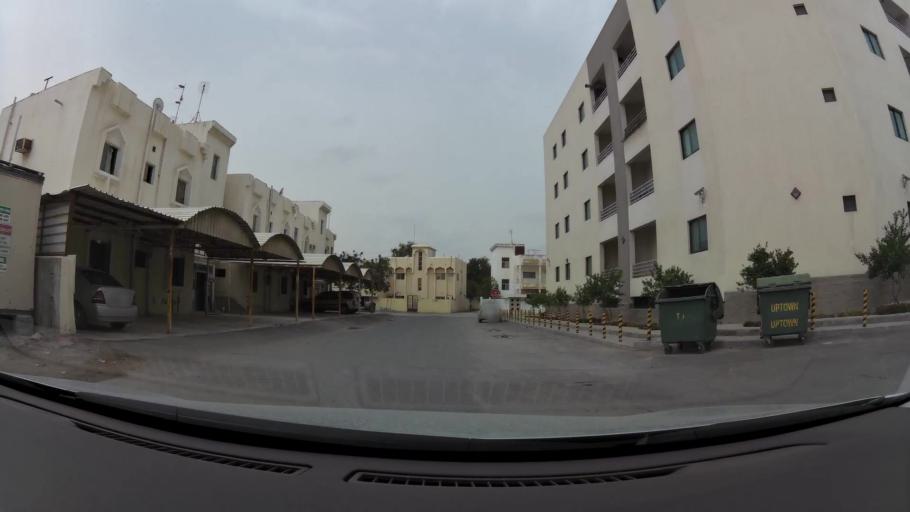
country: QA
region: Baladiyat ad Dawhah
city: Doha
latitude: 25.2534
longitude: 51.5516
